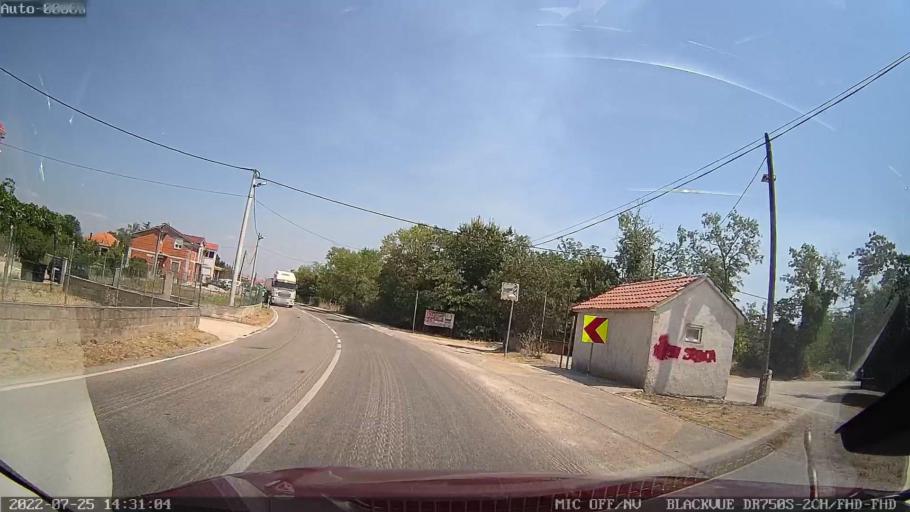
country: HR
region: Zadarska
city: Galovac
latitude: 44.1106
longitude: 15.3683
